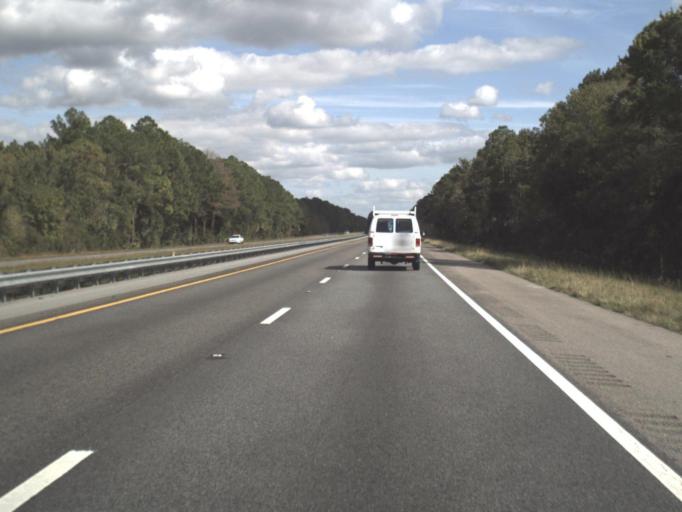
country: US
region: Florida
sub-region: Orange County
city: Christmas
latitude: 28.4526
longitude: -80.9550
